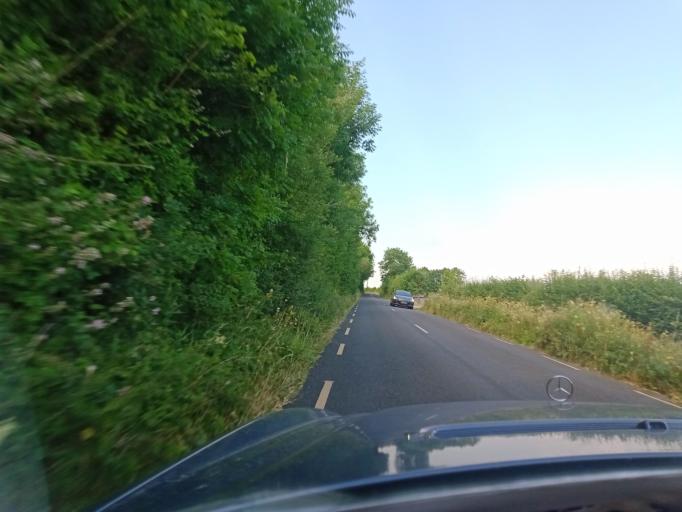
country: IE
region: Leinster
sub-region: Kilkenny
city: Callan
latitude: 52.4975
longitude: -7.3160
